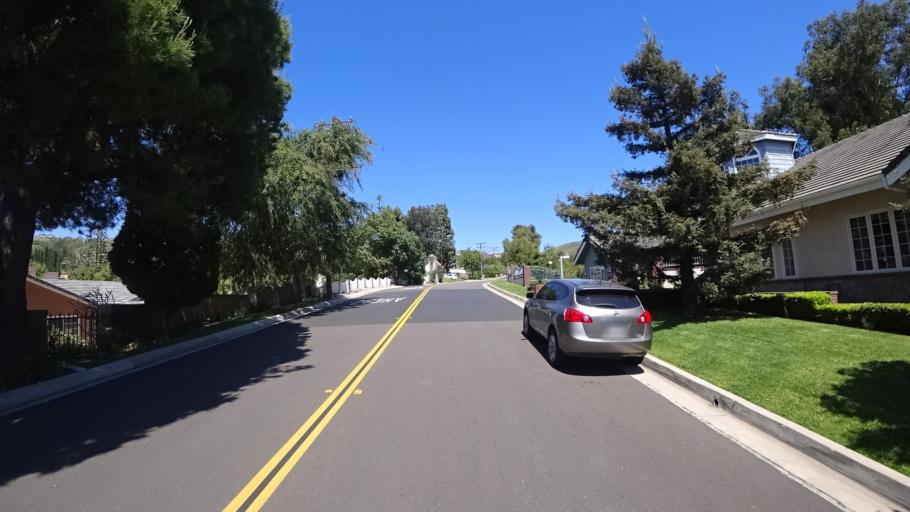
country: US
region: California
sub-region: Orange County
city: Villa Park
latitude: 33.8273
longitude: -117.7999
